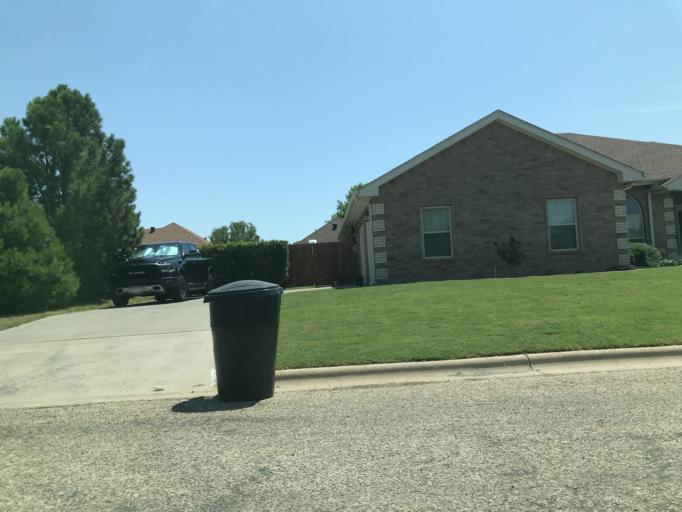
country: US
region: Texas
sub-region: Taylor County
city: Abilene
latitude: 32.4895
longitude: -99.6875
